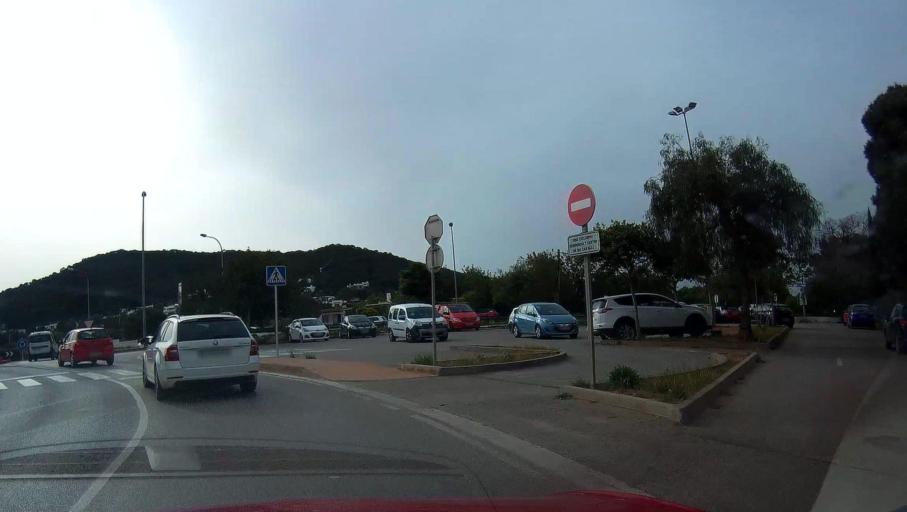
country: ES
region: Balearic Islands
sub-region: Illes Balears
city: Santa Eularia des Riu
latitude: 38.9901
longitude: 1.5413
